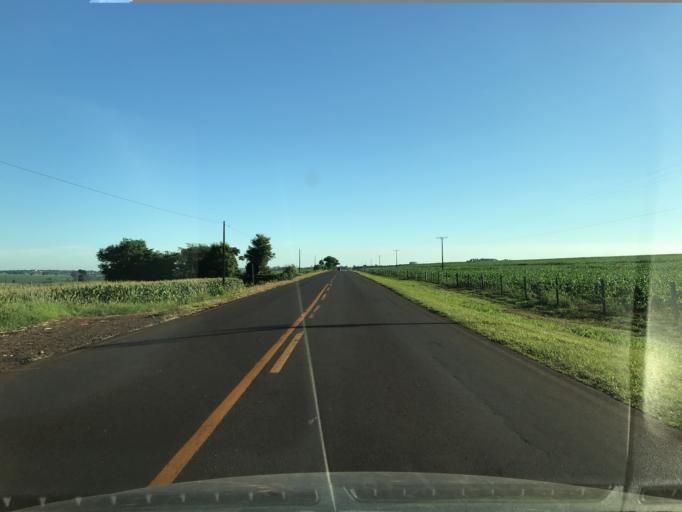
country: BR
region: Parana
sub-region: Palotina
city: Palotina
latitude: -24.1146
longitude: -53.8462
